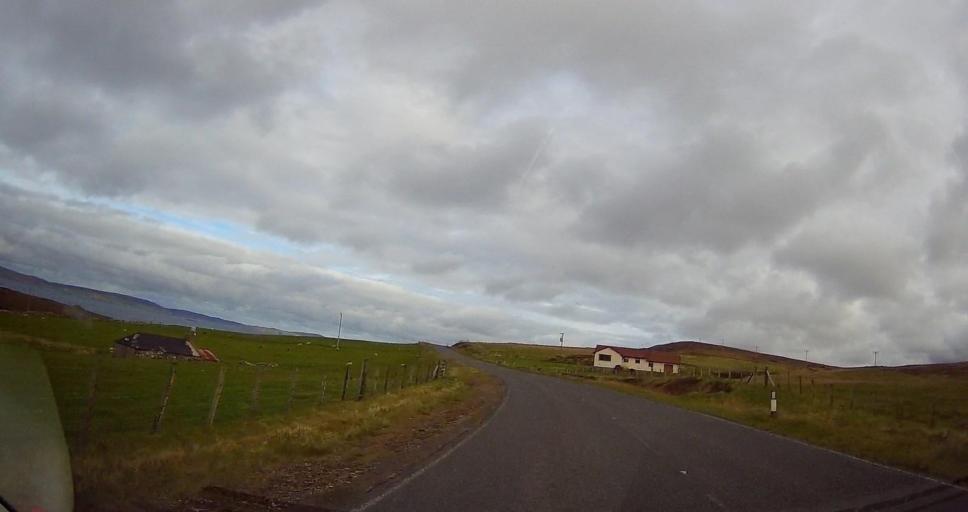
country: GB
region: Scotland
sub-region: Shetland Islands
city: Shetland
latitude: 60.5199
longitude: -1.1639
